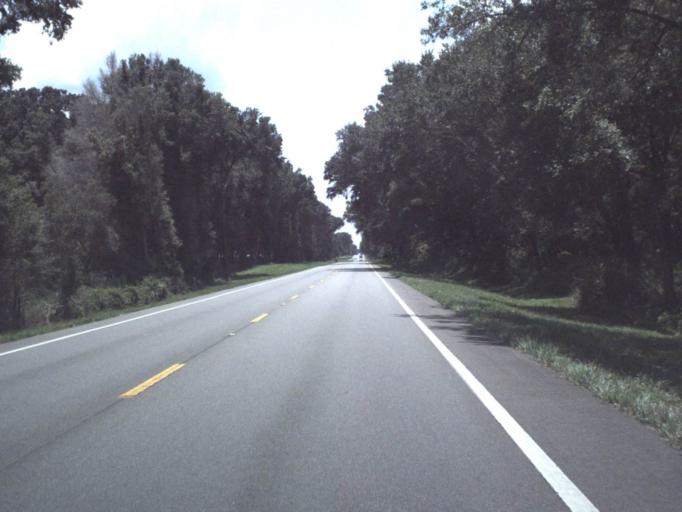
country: US
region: Florida
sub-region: Levy County
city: Williston
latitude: 29.4534
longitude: -82.4729
